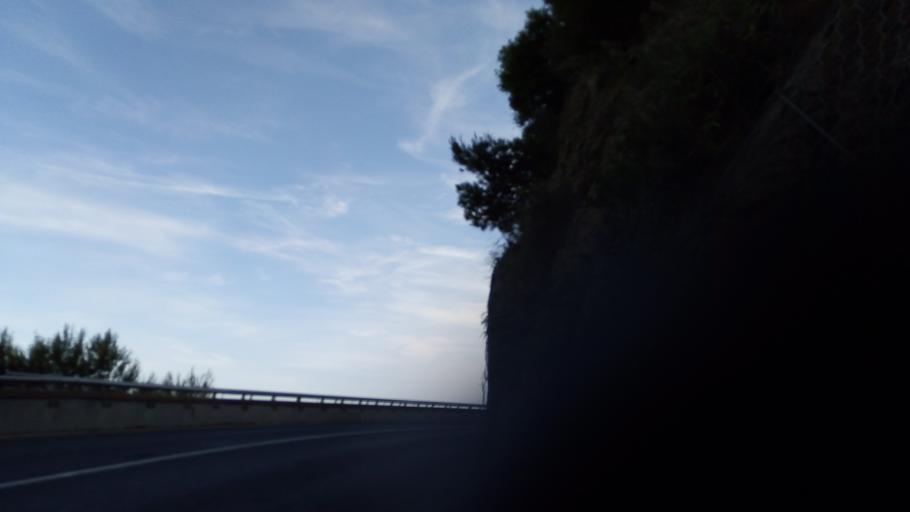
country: IT
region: Liguria
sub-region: Provincia di Savona
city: Borghetto Santo Spirito
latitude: 44.1048
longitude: 8.2389
